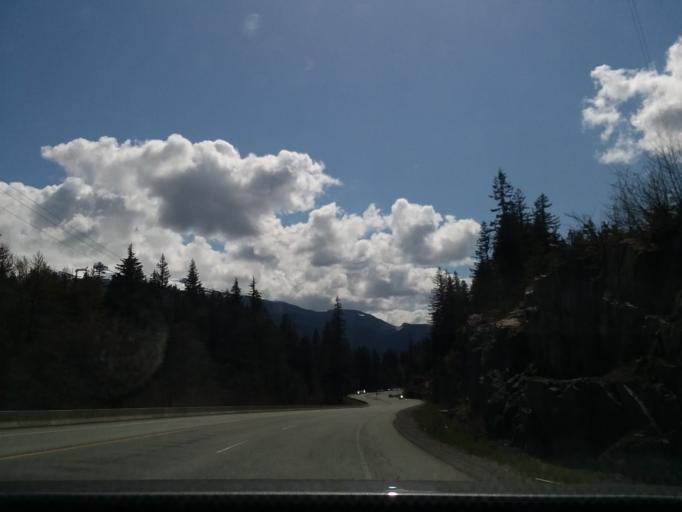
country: CA
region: British Columbia
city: Whistler
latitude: 50.0420
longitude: -123.1236
